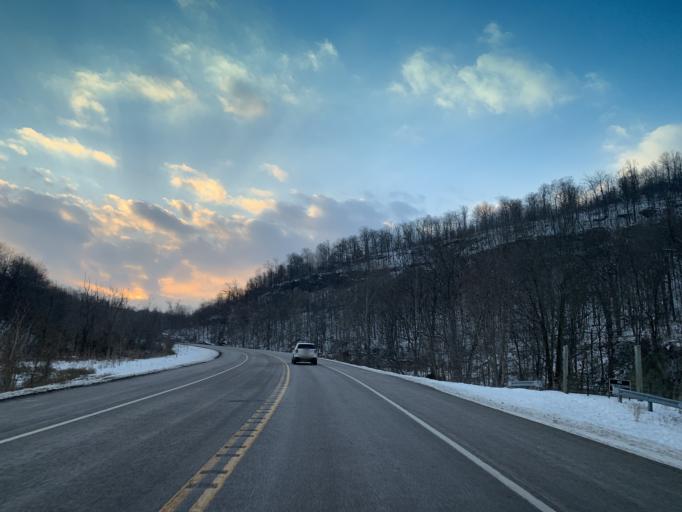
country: US
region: Maryland
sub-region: Allegany County
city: La Vale
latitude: 39.7017
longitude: -78.8344
